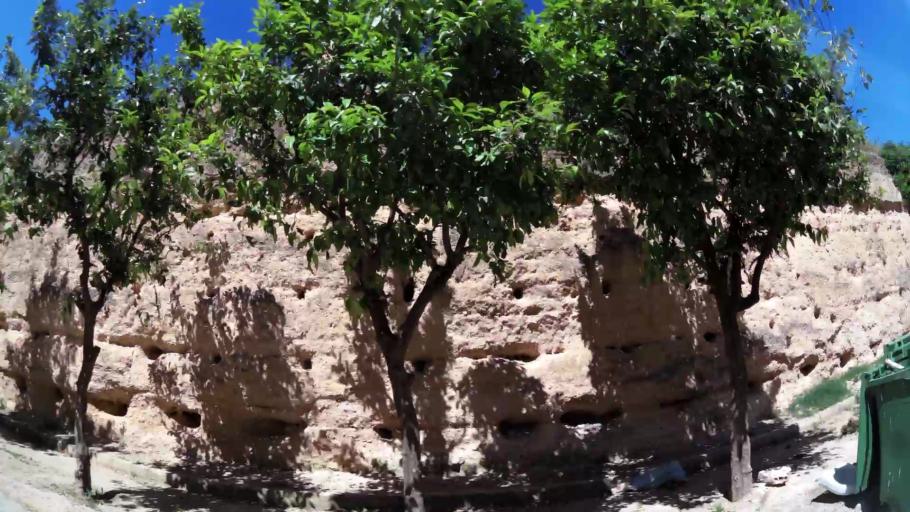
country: MA
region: Meknes-Tafilalet
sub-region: Meknes
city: Meknes
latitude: 33.8803
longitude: -5.5603
